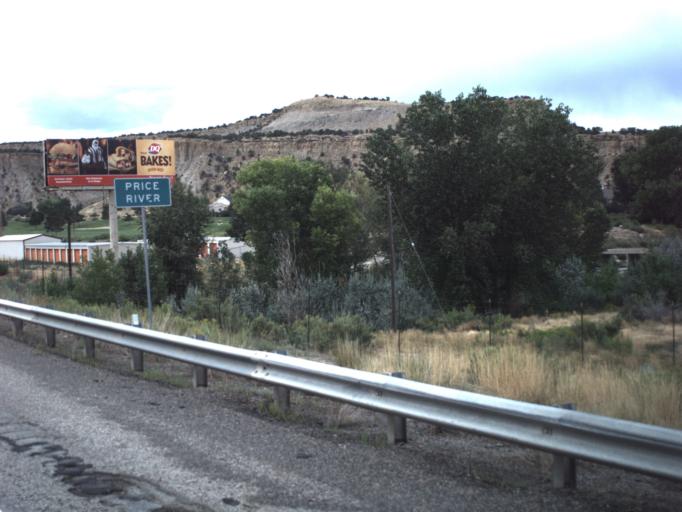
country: US
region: Utah
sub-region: Carbon County
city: Spring Glen
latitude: 39.6398
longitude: -110.8598
